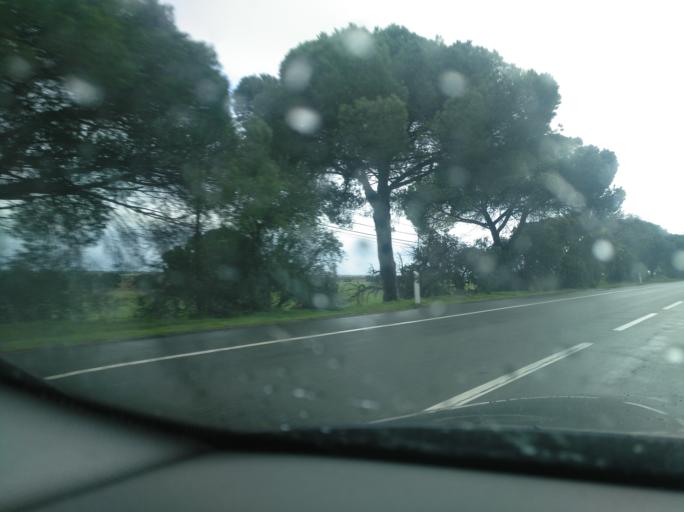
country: PT
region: Setubal
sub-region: Grandola
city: Grandola
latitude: 38.0981
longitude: -8.4184
